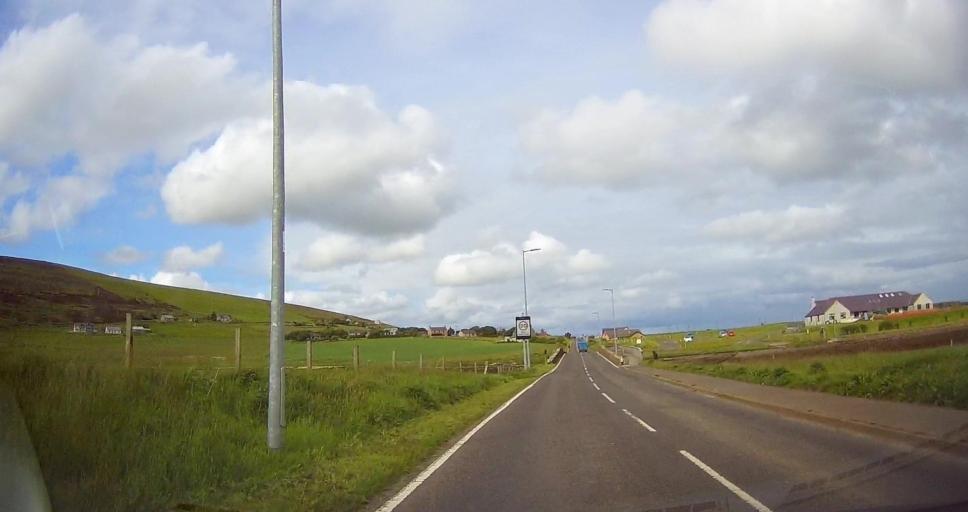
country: GB
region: Scotland
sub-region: Orkney Islands
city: Orkney
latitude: 59.0096
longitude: -3.1143
